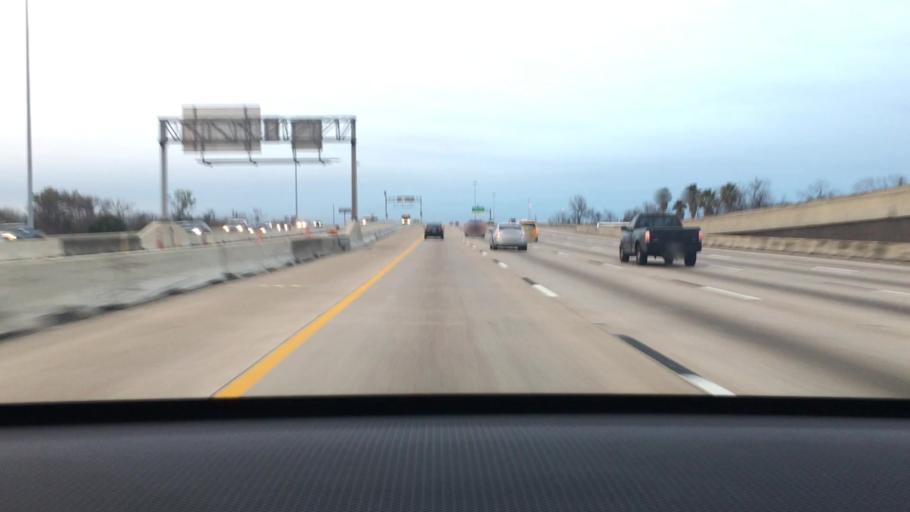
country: US
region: Texas
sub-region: Harris County
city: Aldine
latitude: 29.8561
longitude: -95.3335
